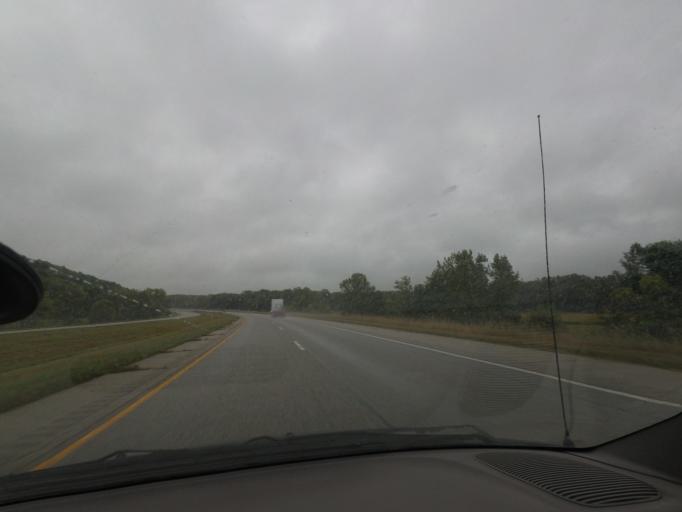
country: US
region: Illinois
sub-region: Pike County
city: Barry
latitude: 39.7139
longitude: -91.1047
